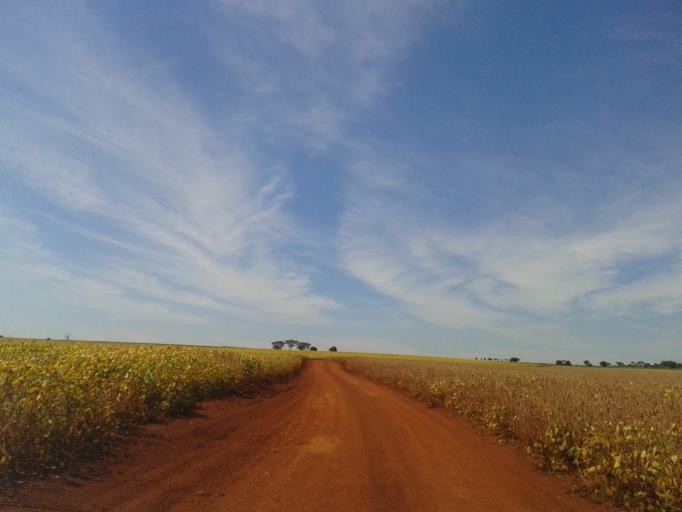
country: BR
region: Minas Gerais
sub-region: Capinopolis
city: Capinopolis
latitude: -18.6529
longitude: -49.7029
